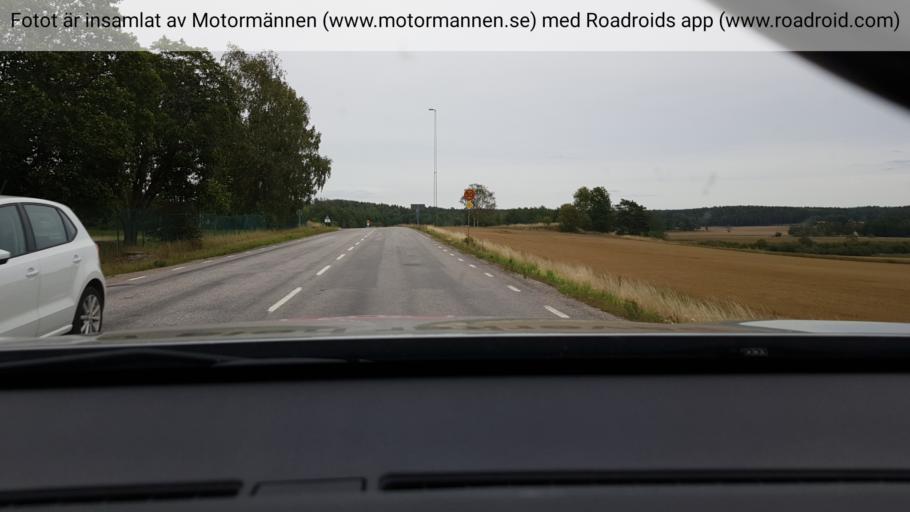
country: SE
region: Soedermanland
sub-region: Gnesta Kommun
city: Gnesta
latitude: 58.9019
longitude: 17.3134
